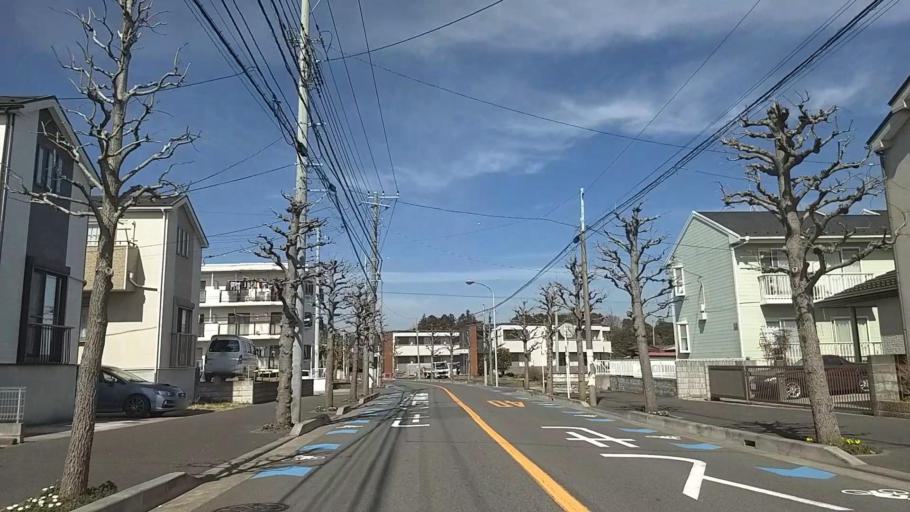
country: JP
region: Kanagawa
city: Fujisawa
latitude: 35.4009
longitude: 139.4725
